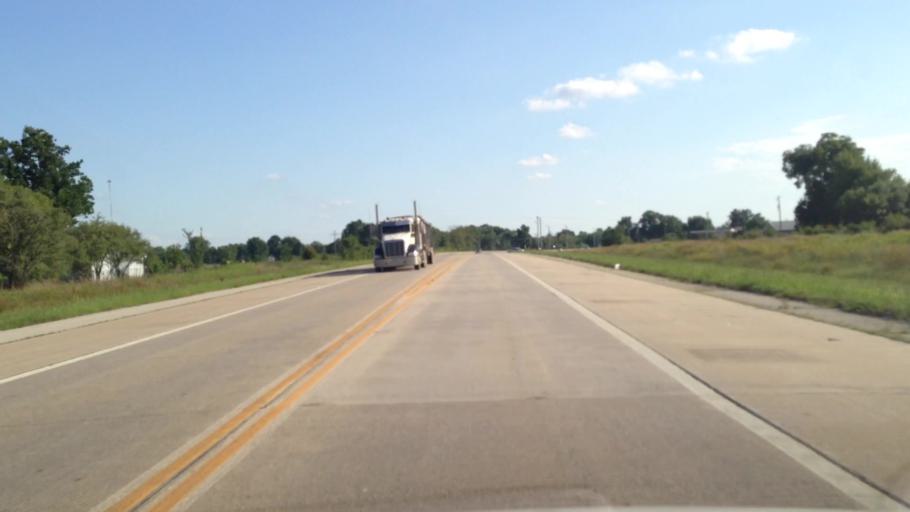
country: US
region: Kansas
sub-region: Crawford County
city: Arma
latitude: 37.5607
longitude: -94.7046
